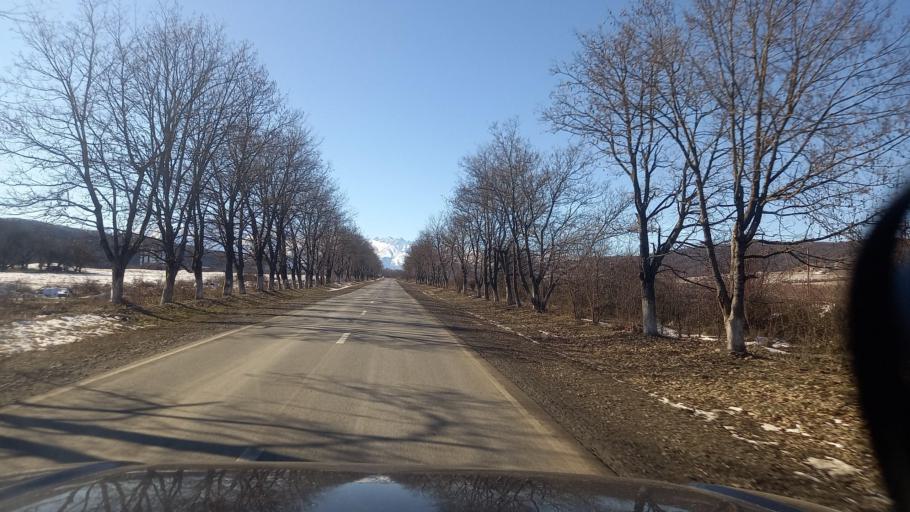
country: RU
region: Kabardino-Balkariya
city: Urukh
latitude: 43.2513
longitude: 43.9734
